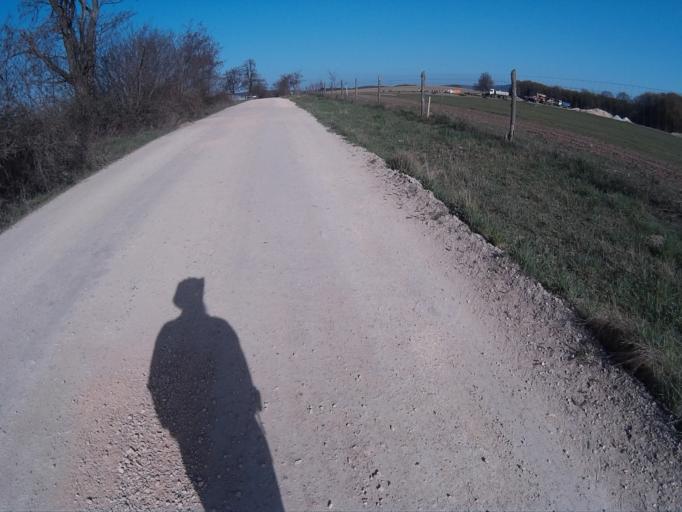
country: HU
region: Veszprem
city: Herend
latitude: 47.1923
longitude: 17.8000
